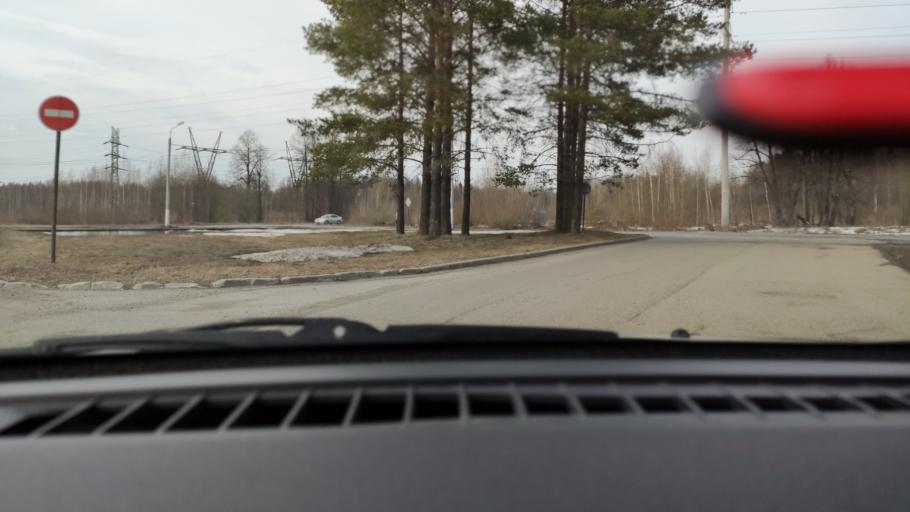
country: RU
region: Perm
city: Perm
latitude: 58.0941
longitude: 56.4029
